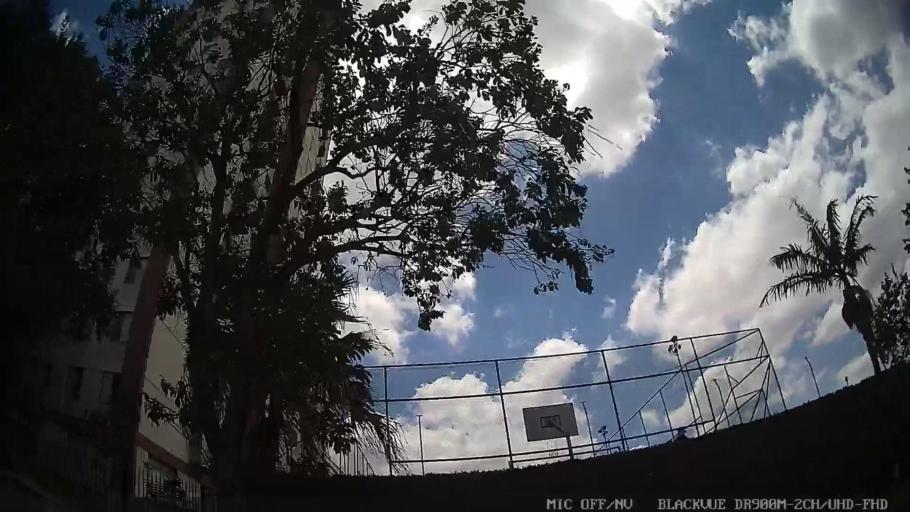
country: BR
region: Sao Paulo
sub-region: Diadema
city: Diadema
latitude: -23.6570
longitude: -46.6487
